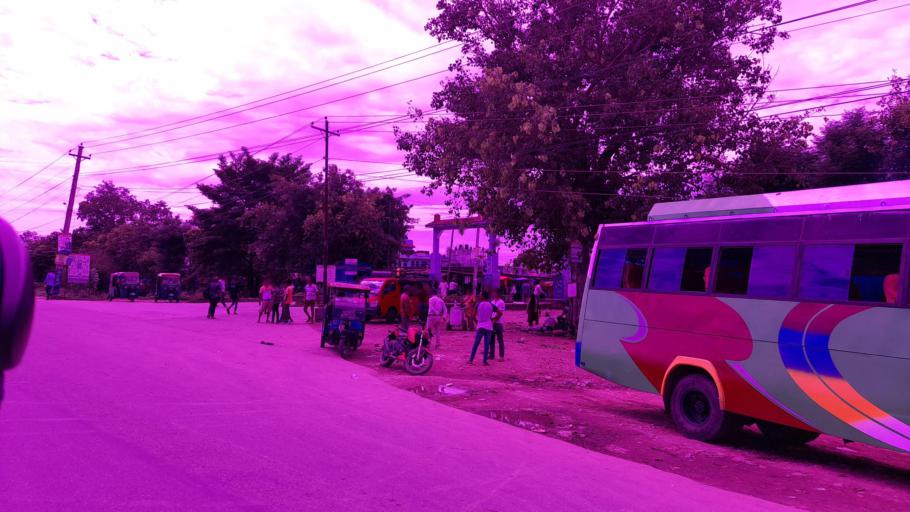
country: NP
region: Mid Western
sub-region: Bheri Zone
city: Nepalgunj
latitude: 28.1998
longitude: 81.6864
